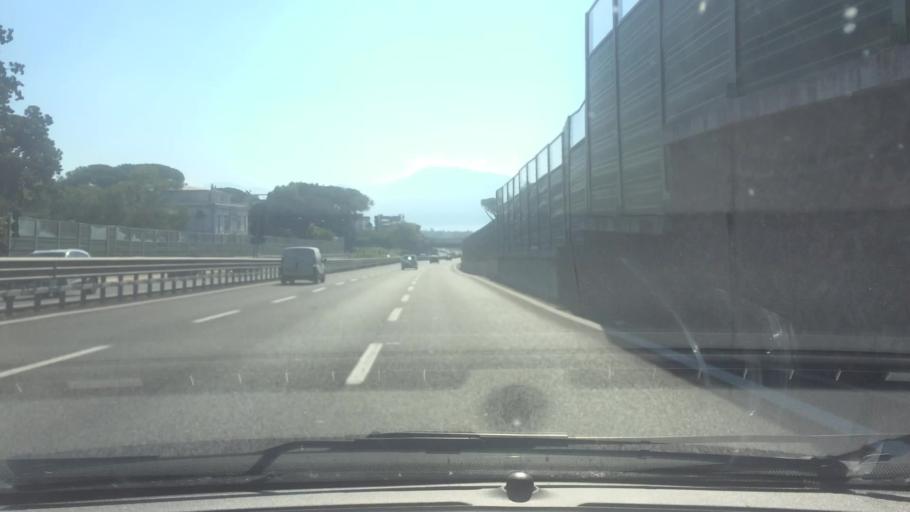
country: IT
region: Campania
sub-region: Provincia di Napoli
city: Ercolano
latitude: 40.7964
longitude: 14.3734
